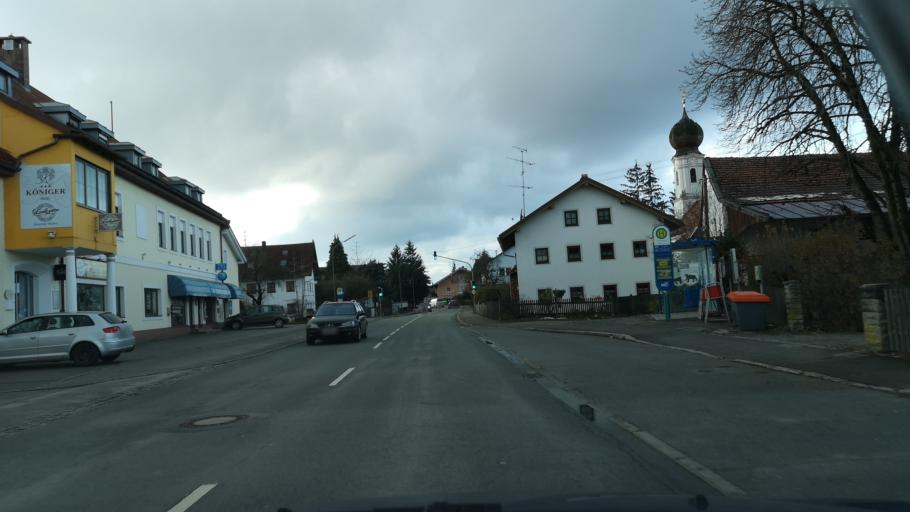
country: DE
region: Bavaria
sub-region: Upper Bavaria
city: Kirchheim bei Muenchen
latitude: 48.1882
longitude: 11.7769
